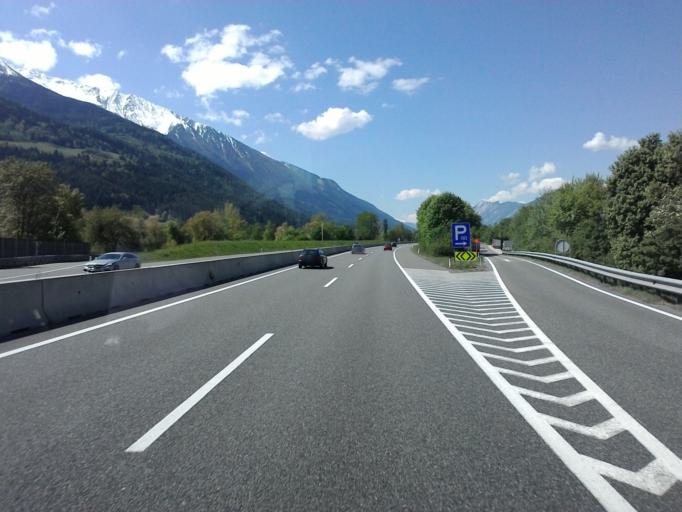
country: AT
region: Tyrol
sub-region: Politischer Bezirk Innsbruck Land
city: Pfaffenhofen
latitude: 47.3047
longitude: 11.0865
